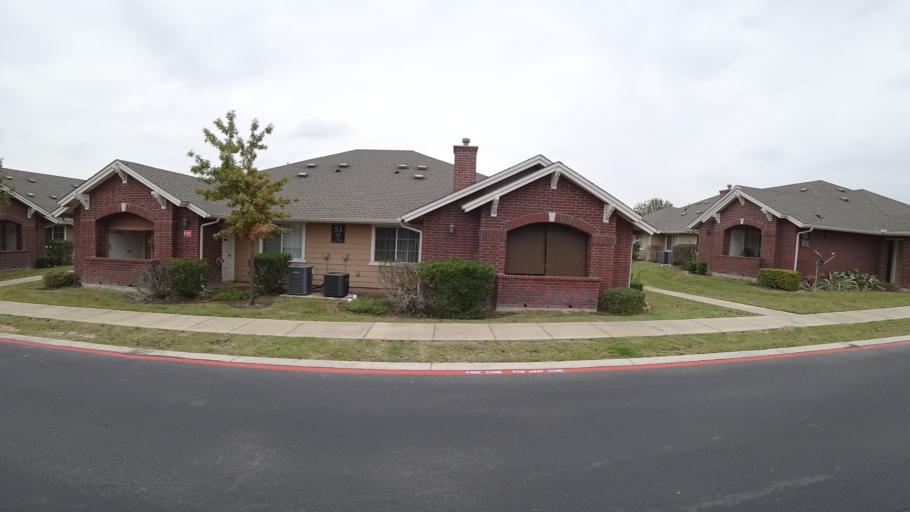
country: US
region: Texas
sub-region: Travis County
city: Pflugerville
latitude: 30.4299
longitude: -97.6209
